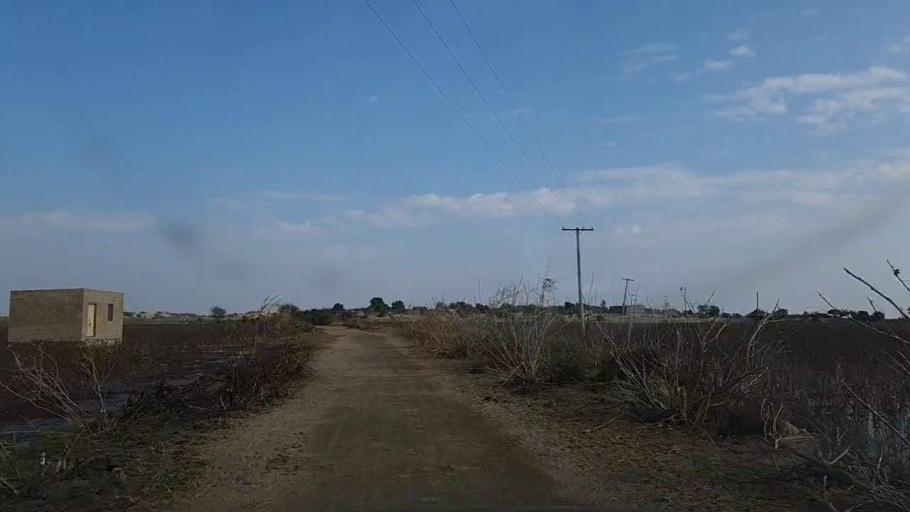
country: PK
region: Sindh
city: Sanghar
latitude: 26.2039
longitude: 69.0232
